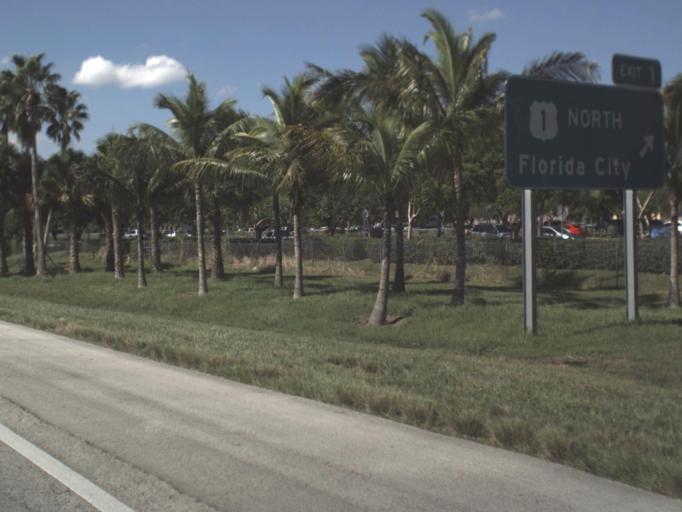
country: US
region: Florida
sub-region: Miami-Dade County
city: Florida City
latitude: 25.4566
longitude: -80.4710
